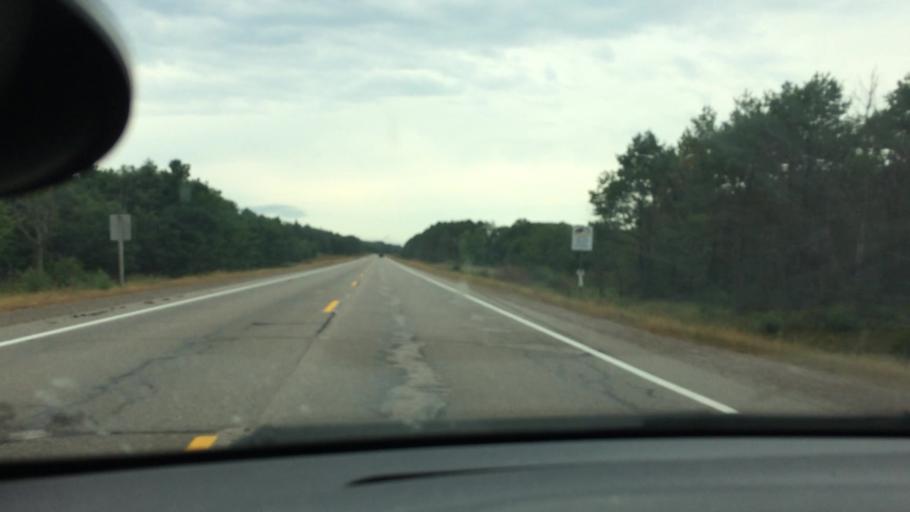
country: US
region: Wisconsin
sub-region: Eau Claire County
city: Augusta
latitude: 44.5805
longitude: -91.0657
